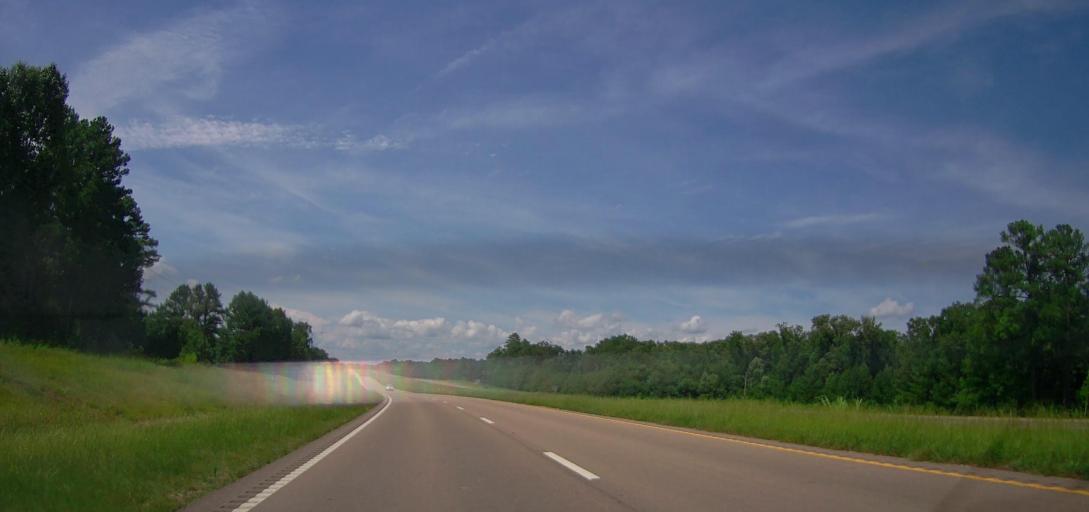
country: US
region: Mississippi
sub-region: Monroe County
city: Amory
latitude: 33.9389
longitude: -88.5978
